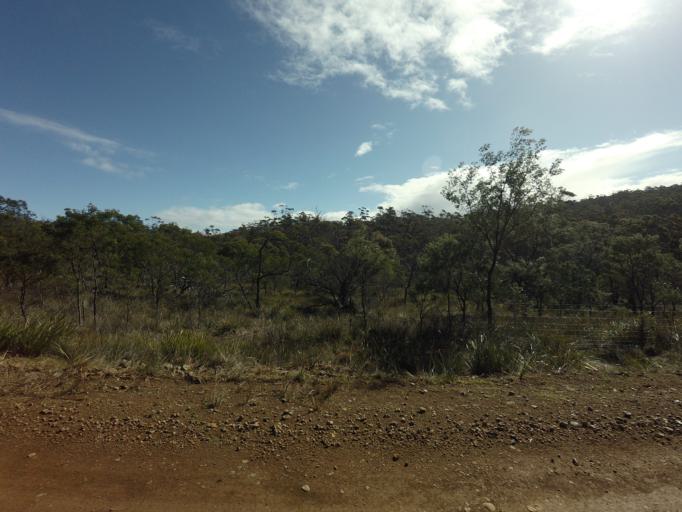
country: AU
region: Tasmania
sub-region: Sorell
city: Sorell
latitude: -42.4064
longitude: 147.9549
